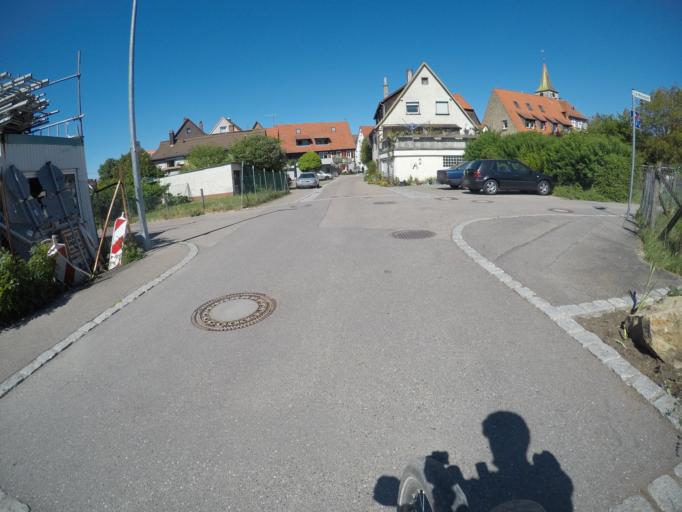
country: DE
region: Baden-Wuerttemberg
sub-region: Regierungsbezirk Stuttgart
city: Leonberg
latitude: 48.7879
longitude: 9.0044
